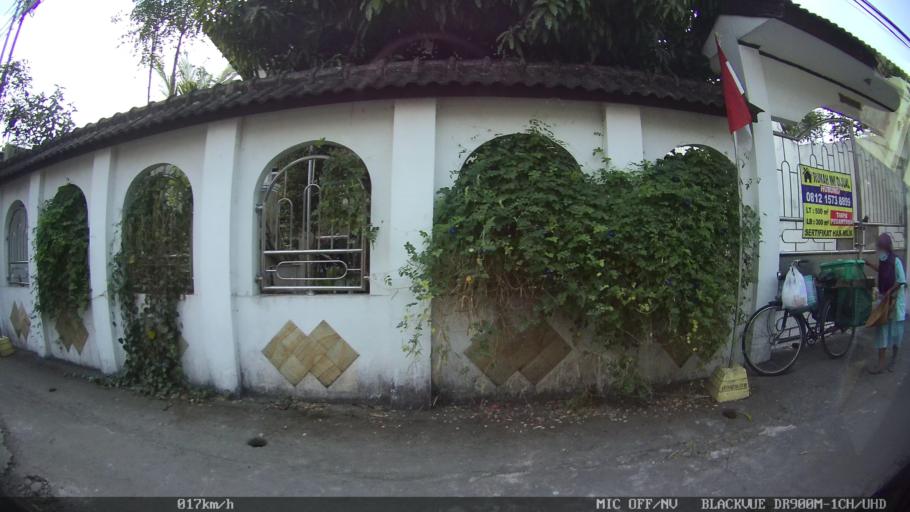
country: ID
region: Daerah Istimewa Yogyakarta
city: Yogyakarta
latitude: -7.8128
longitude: 110.4037
